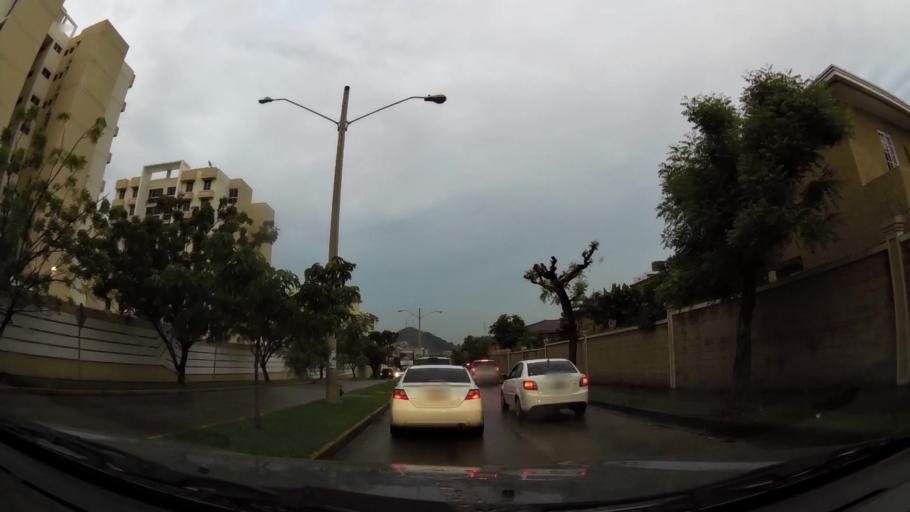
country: PA
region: Panama
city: Panama
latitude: 9.0359
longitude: -79.5311
